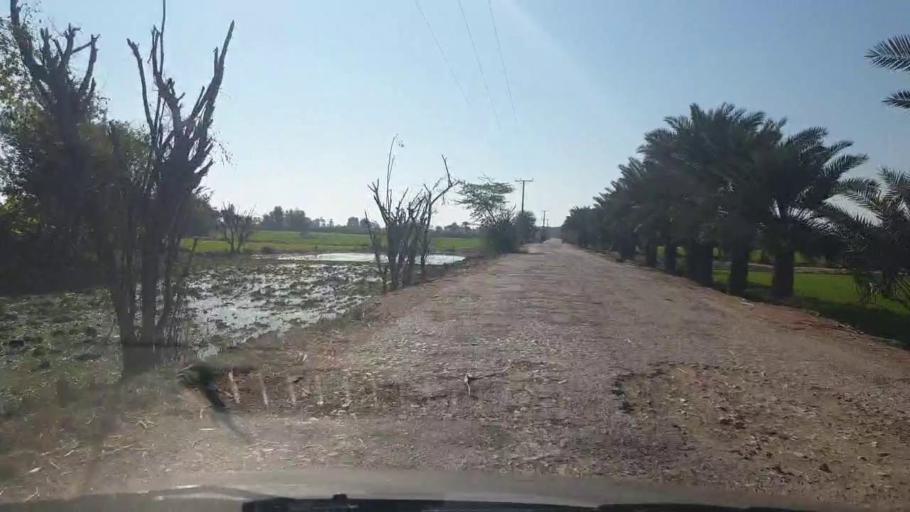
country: PK
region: Sindh
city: Bozdar
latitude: 27.2562
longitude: 68.6525
